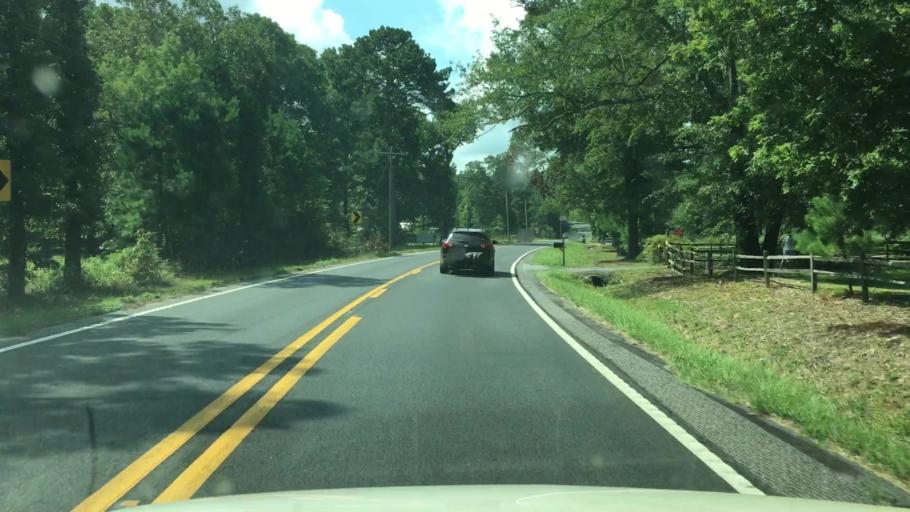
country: US
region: Arkansas
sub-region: Clark County
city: Arkadelphia
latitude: 34.2619
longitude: -93.1301
